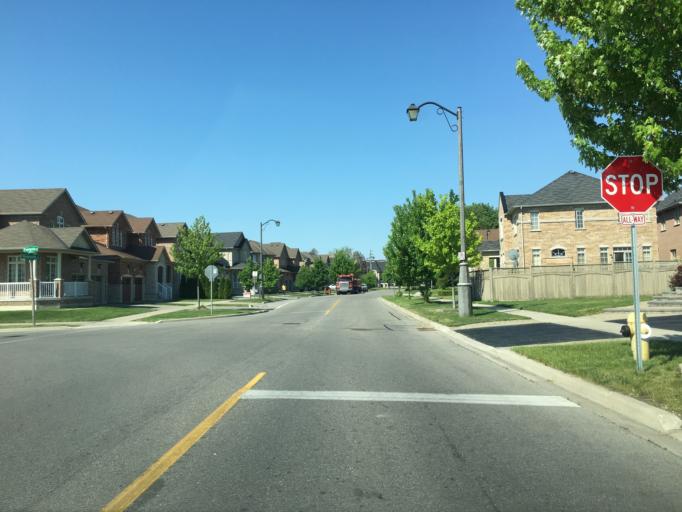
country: CA
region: Ontario
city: Markham
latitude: 43.8562
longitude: -79.2268
